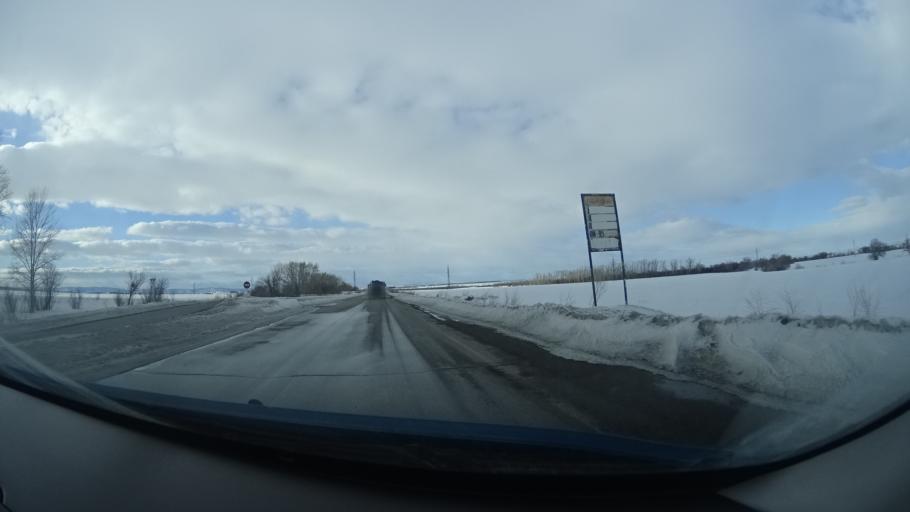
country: RU
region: Chelyabinsk
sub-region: Gorod Magnitogorsk
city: Magnitogorsk
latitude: 53.5820
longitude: 58.8857
